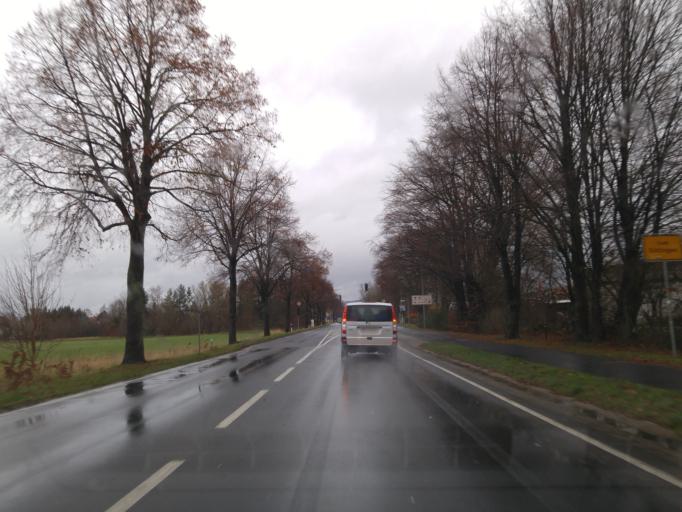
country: DE
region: Lower Saxony
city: Goettingen
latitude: 51.5109
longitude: 9.9392
